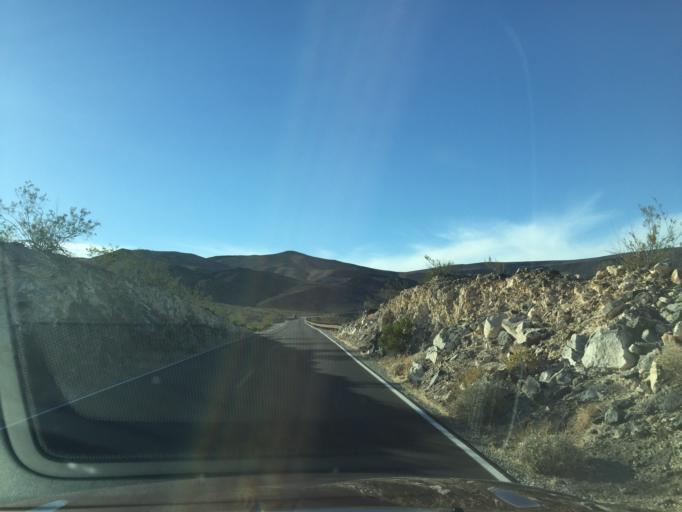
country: US
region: California
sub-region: San Bernardino County
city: Searles Valley
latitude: 36.3466
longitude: -117.5221
